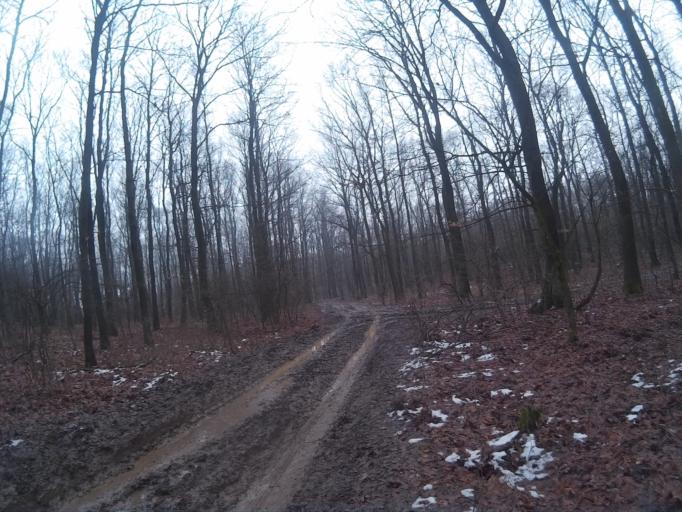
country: HU
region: Komarom-Esztergom
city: Tardos
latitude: 47.6457
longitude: 18.4743
